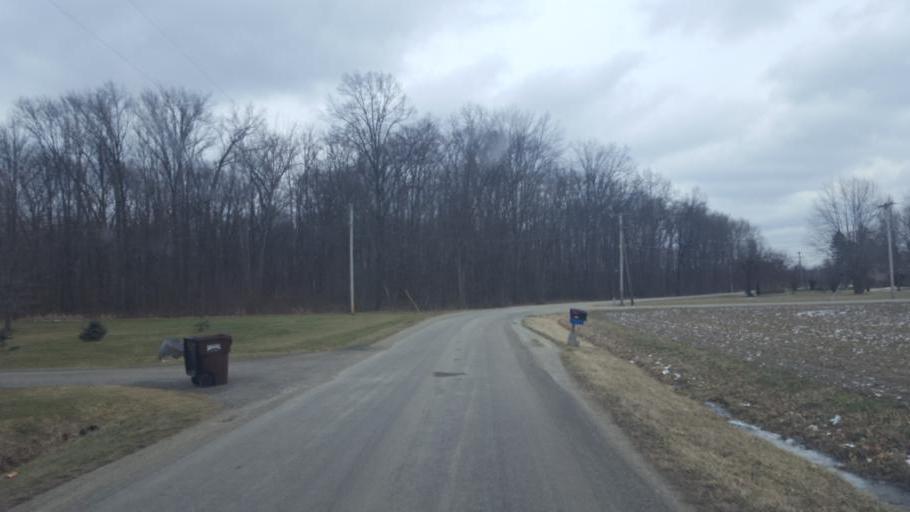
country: US
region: Ohio
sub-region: Crawford County
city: Crestline
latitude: 40.7502
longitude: -82.6896
